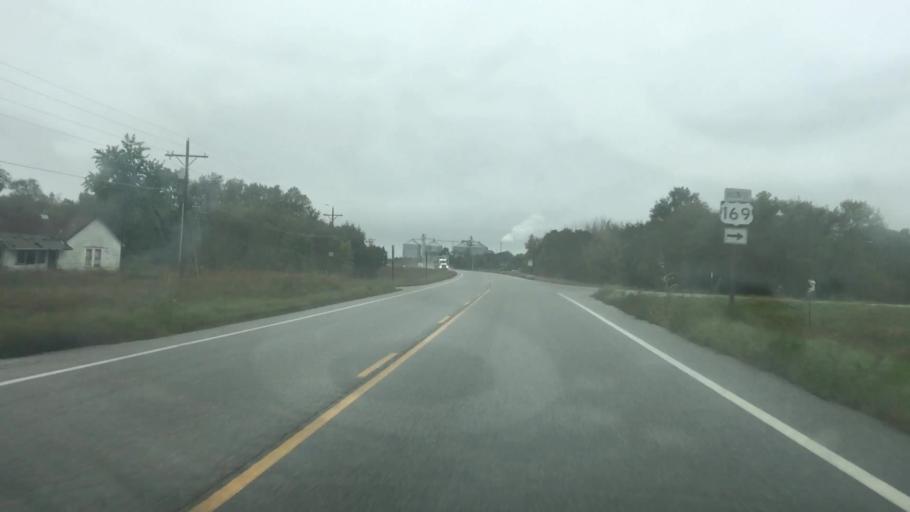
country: US
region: Kansas
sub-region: Anderson County
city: Garnett
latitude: 38.2791
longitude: -95.2237
